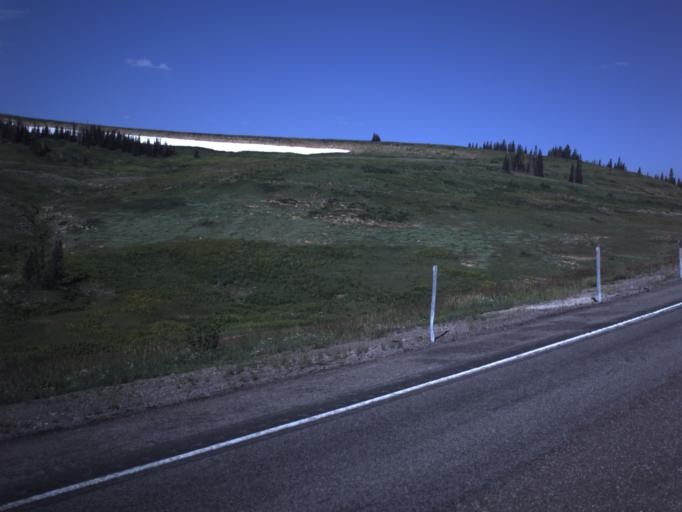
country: US
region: Utah
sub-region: Sanpete County
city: Fairview
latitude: 39.6184
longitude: -111.2832
